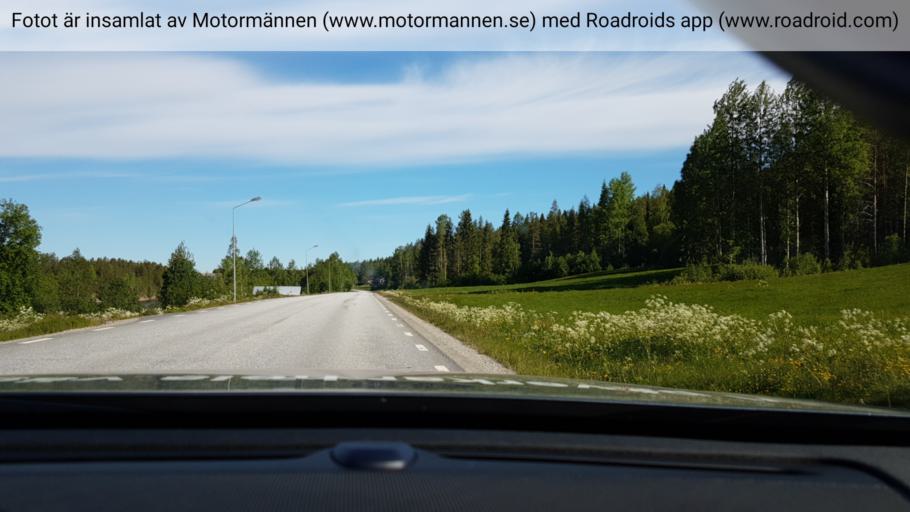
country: SE
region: Vaesterbotten
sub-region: Vindelns Kommun
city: Vindeln
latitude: 64.1453
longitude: 19.5167
